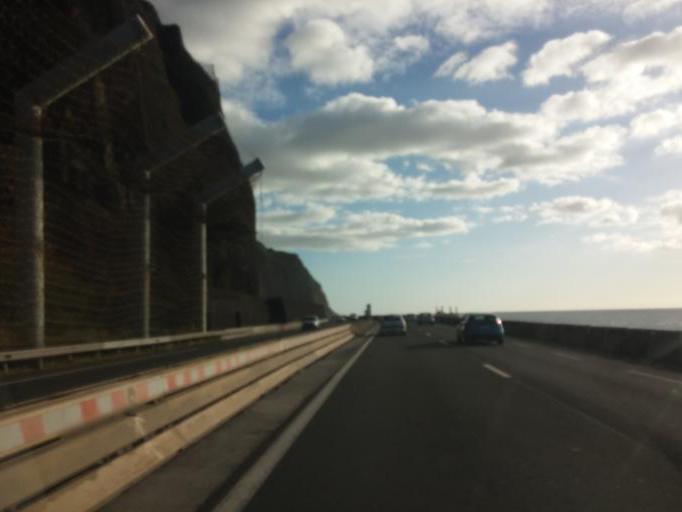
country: RE
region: Reunion
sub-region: Reunion
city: Saint-Denis
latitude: -20.8758
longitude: 55.4177
